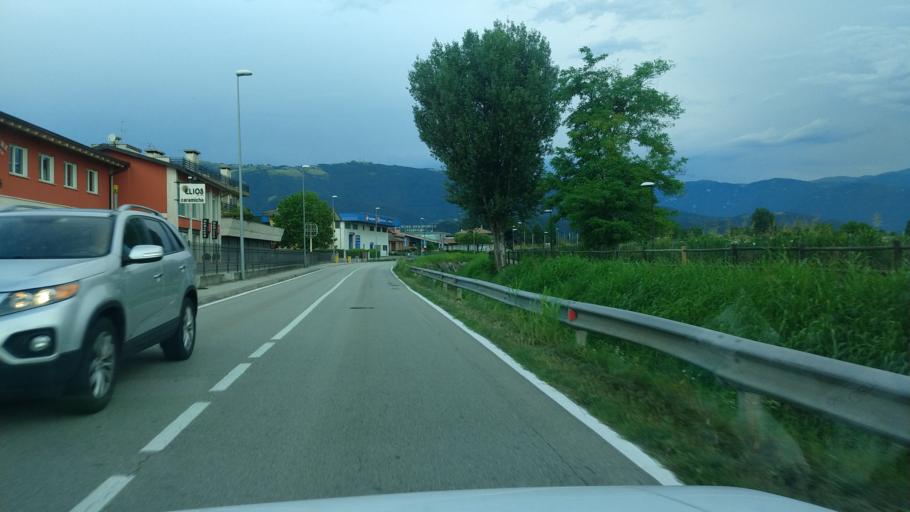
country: IT
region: Veneto
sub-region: Provincia di Vicenza
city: Nove
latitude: 45.7404
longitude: 11.6891
